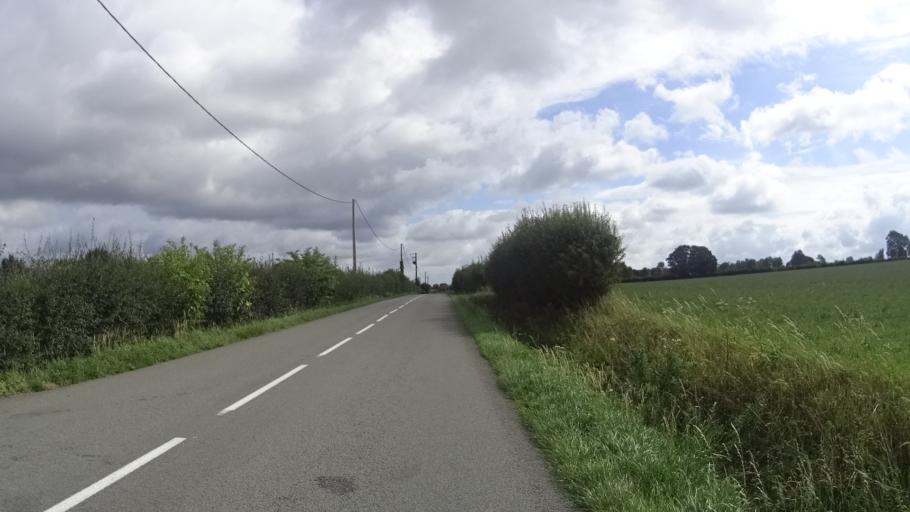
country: FR
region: Nord-Pas-de-Calais
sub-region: Departement du Nord
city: Landrecies
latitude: 50.1053
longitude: 3.6613
